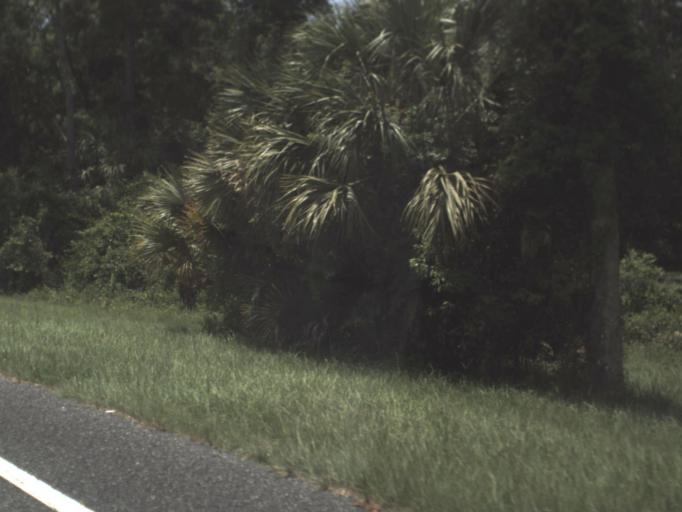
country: US
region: Florida
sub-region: Taylor County
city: Steinhatchee
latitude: 29.7572
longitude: -83.3222
